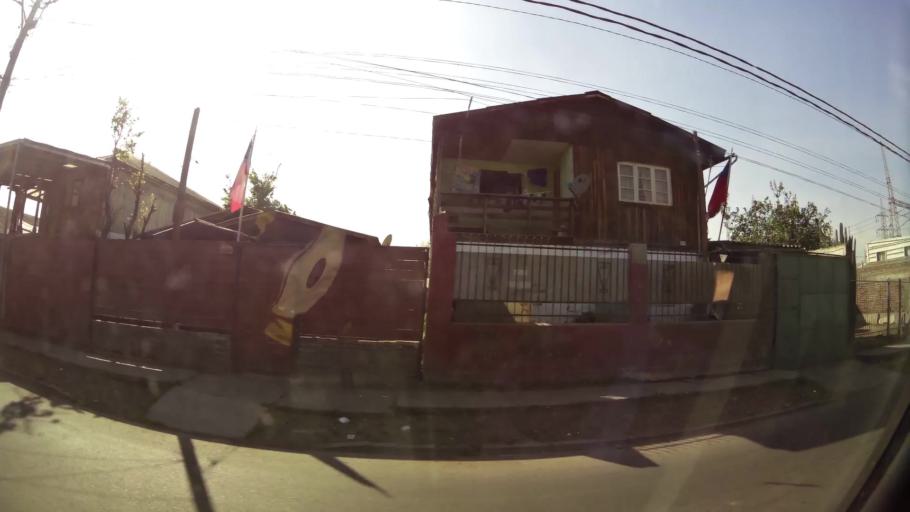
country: CL
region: Santiago Metropolitan
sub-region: Provincia de Santiago
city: Lo Prado
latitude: -33.4208
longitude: -70.7329
